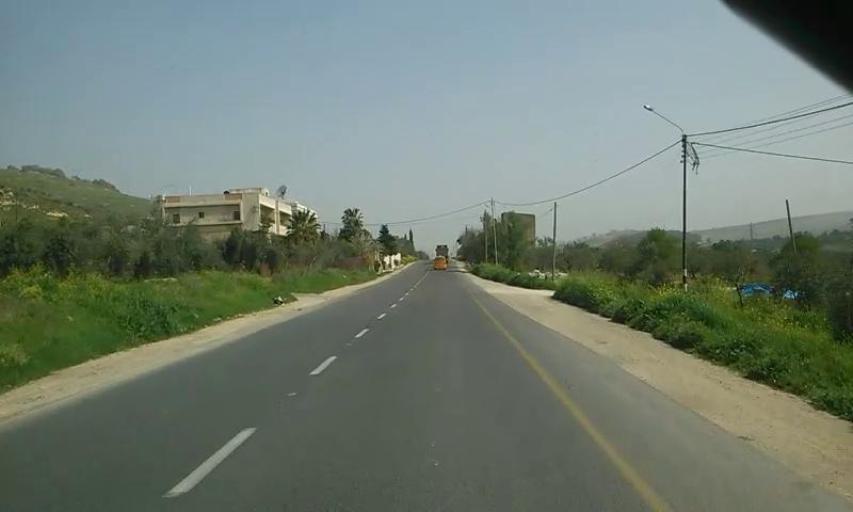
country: PS
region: West Bank
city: Udalah
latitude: 32.1686
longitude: 35.2669
